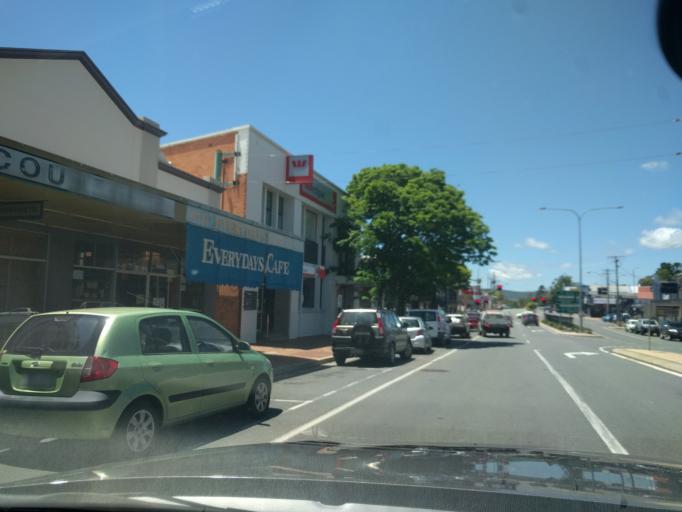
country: AU
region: Queensland
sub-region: Logan
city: Cedar Vale
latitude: -27.9872
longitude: 152.9958
